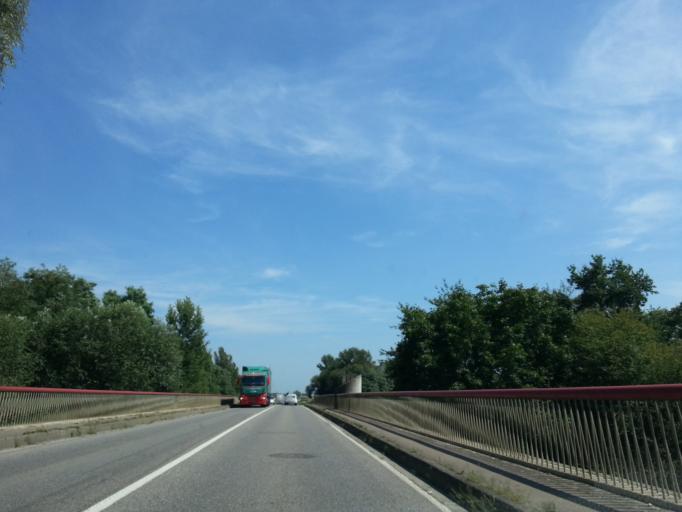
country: FR
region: Alsace
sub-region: Departement du Haut-Rhin
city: Andolsheim
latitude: 48.0678
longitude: 7.4043
